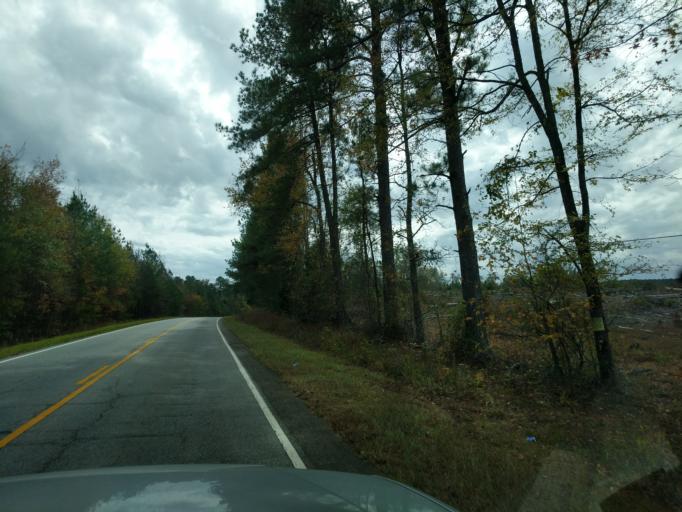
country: US
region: South Carolina
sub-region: Saluda County
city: Saluda
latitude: 34.1554
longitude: -81.8504
